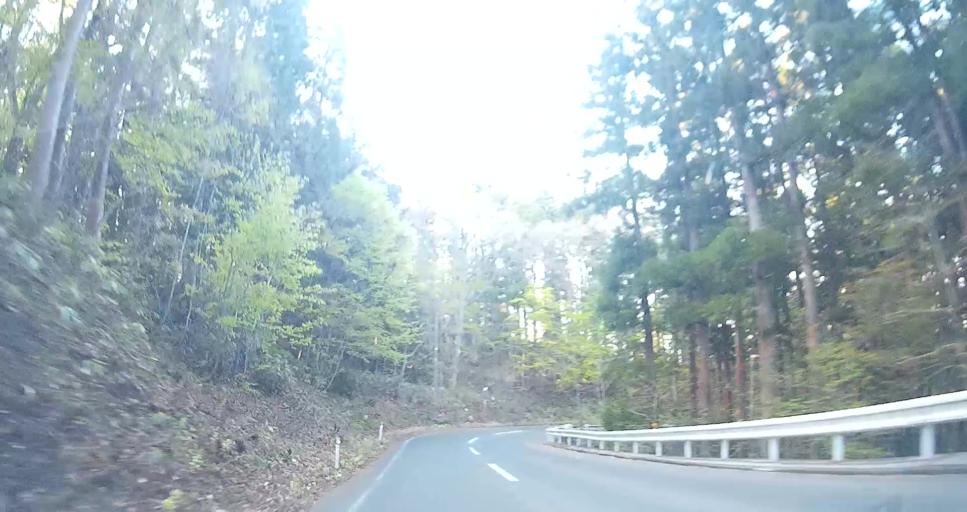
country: JP
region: Aomori
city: Mutsu
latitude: 41.3189
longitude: 141.1394
